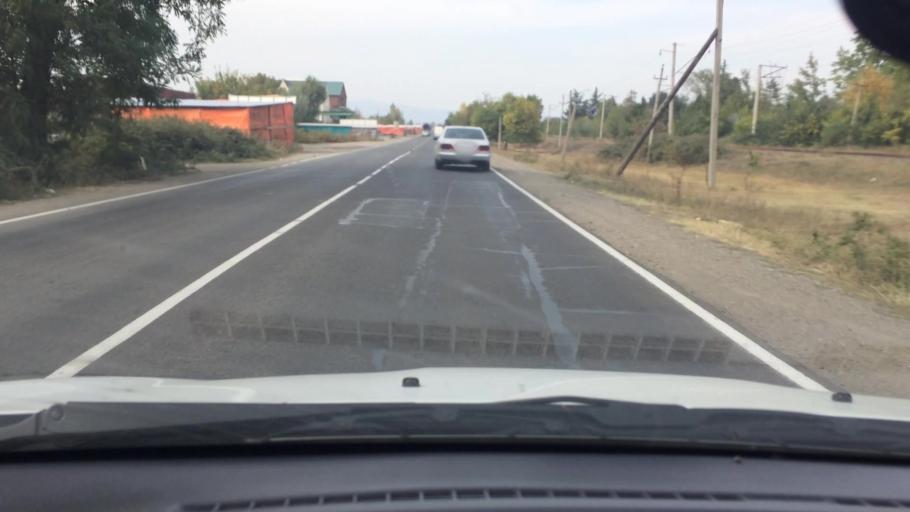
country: GE
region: Kvemo Kartli
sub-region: Marneuli
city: Marneuli
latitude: 41.4171
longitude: 44.8263
